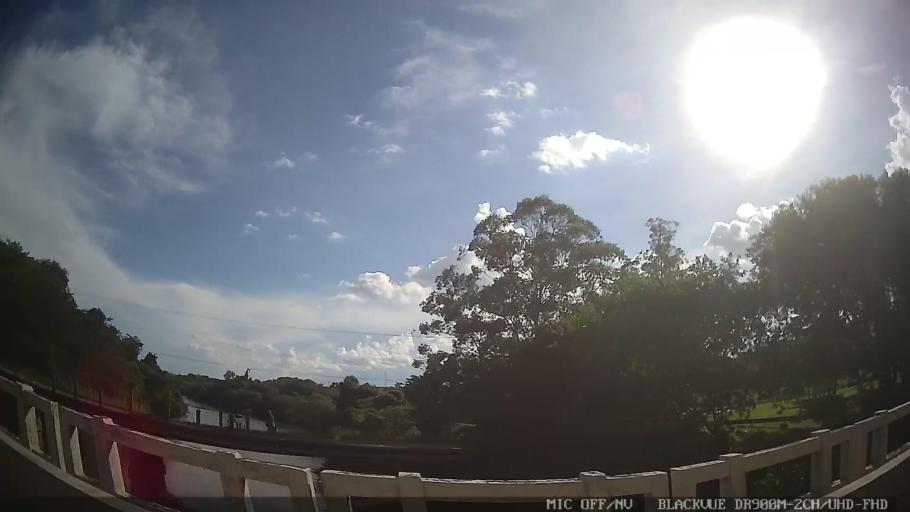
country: BR
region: Sao Paulo
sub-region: Laranjal Paulista
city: Laranjal Paulista
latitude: -23.0652
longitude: -47.8201
